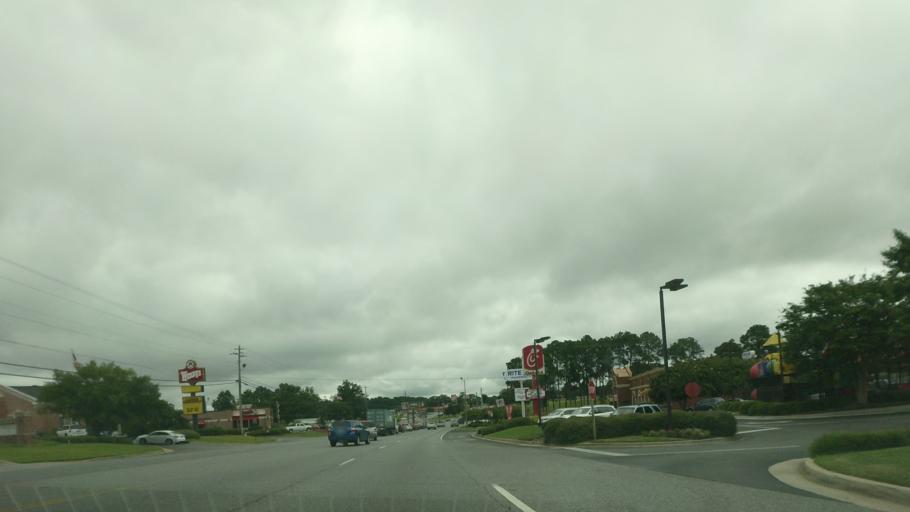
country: US
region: Georgia
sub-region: Laurens County
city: Dublin
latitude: 32.5411
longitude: -82.9485
